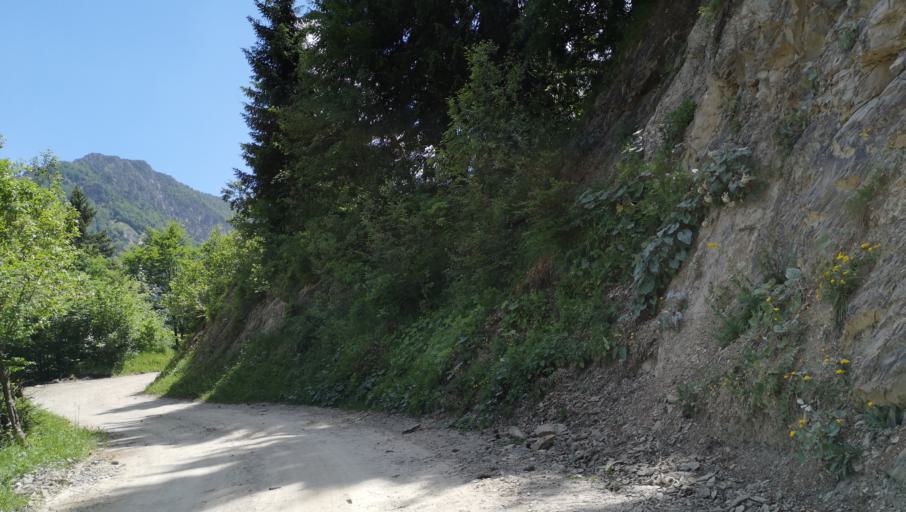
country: IT
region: Friuli Venezia Giulia
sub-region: Provincia di Udine
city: Pontebba
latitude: 46.5089
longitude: 13.2496
